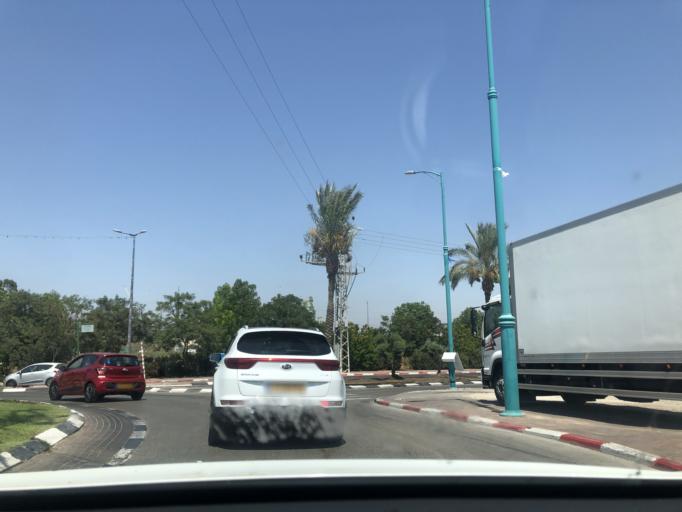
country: IL
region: Central District
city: Lod
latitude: 31.9547
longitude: 34.9046
